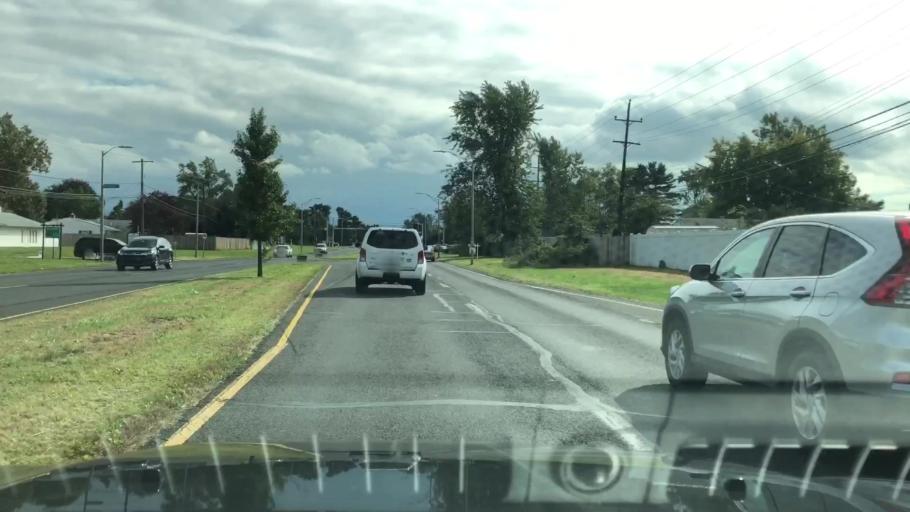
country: US
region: Pennsylvania
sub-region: Bucks County
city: Levittown
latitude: 40.1577
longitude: -74.8304
